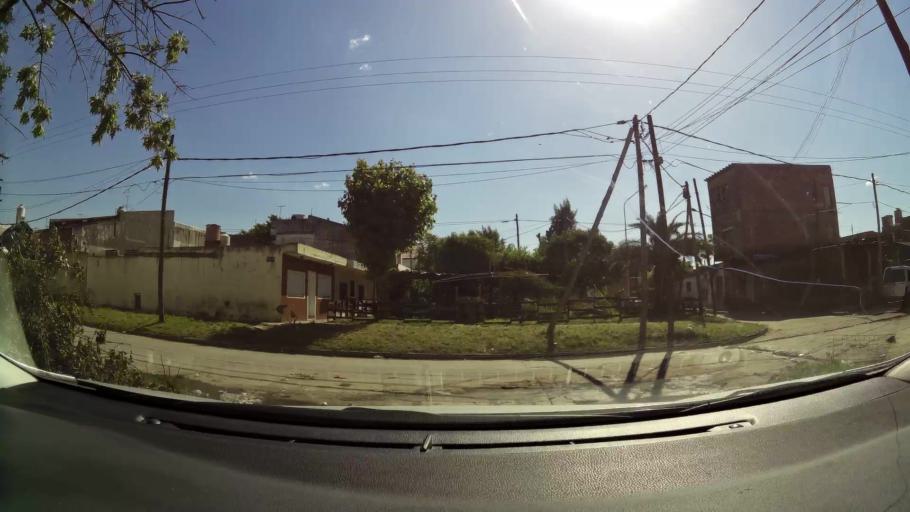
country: AR
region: Buenos Aires F.D.
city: Villa Lugano
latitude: -34.7067
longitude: -58.4761
